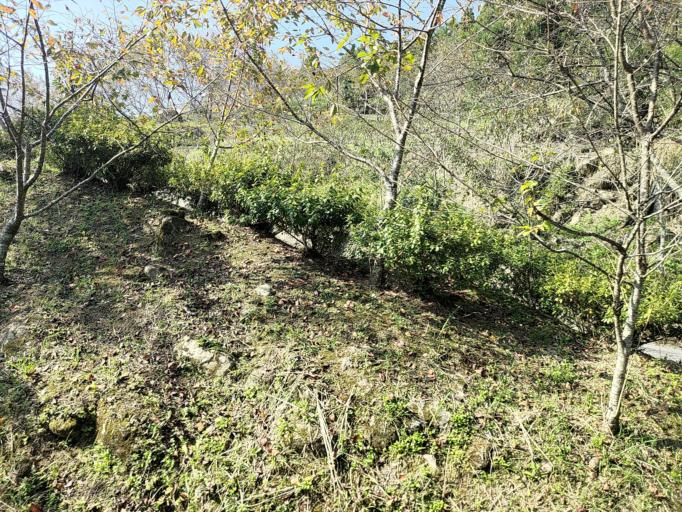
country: TW
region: Taiwan
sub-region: Hsinchu
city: Hsinchu
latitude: 24.6094
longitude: 121.0985
